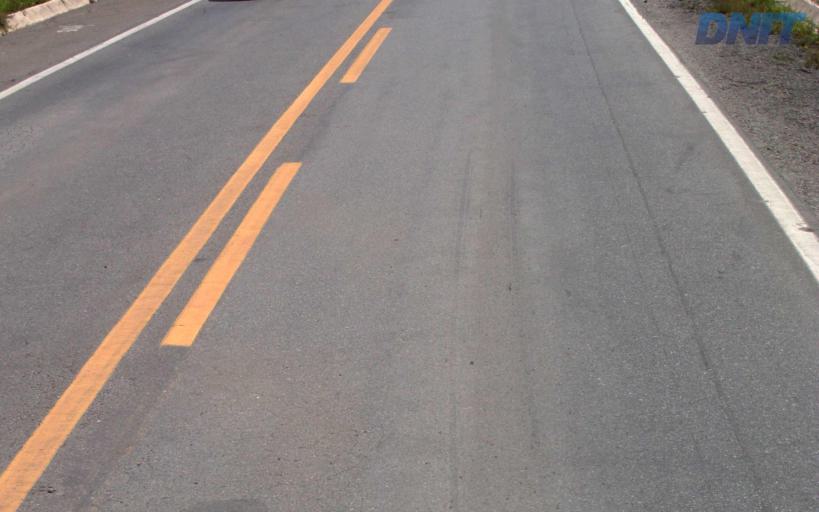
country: BR
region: Minas Gerais
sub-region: Governador Valadares
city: Governador Valadares
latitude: -19.0627
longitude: -42.1627
